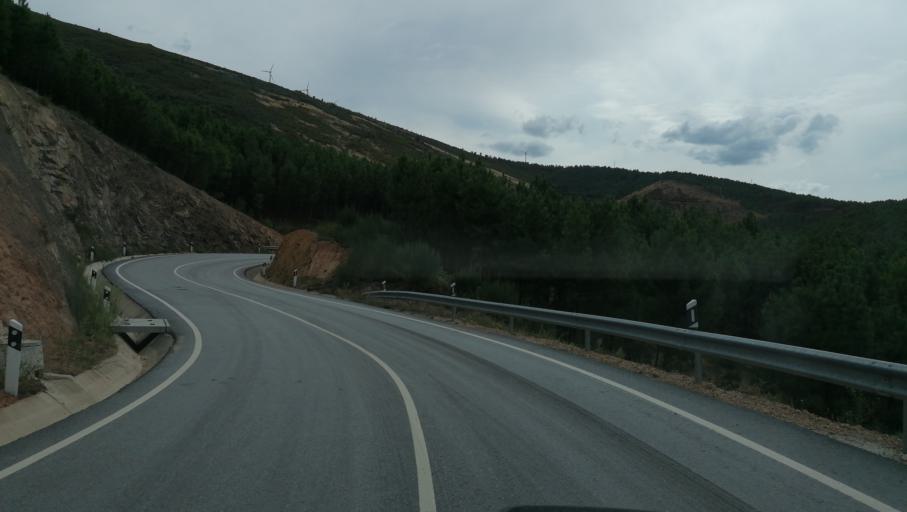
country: PT
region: Vila Real
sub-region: Vila Pouca de Aguiar
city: Vila Pouca de Aguiar
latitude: 41.5570
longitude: -7.7084
